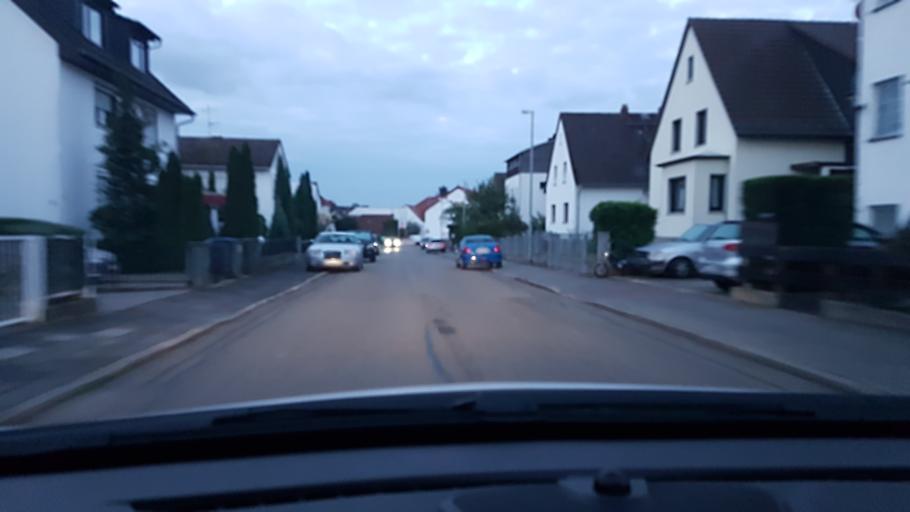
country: DE
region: Hesse
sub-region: Regierungsbezirk Darmstadt
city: Steinbach am Taunus
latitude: 50.1845
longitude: 8.5954
